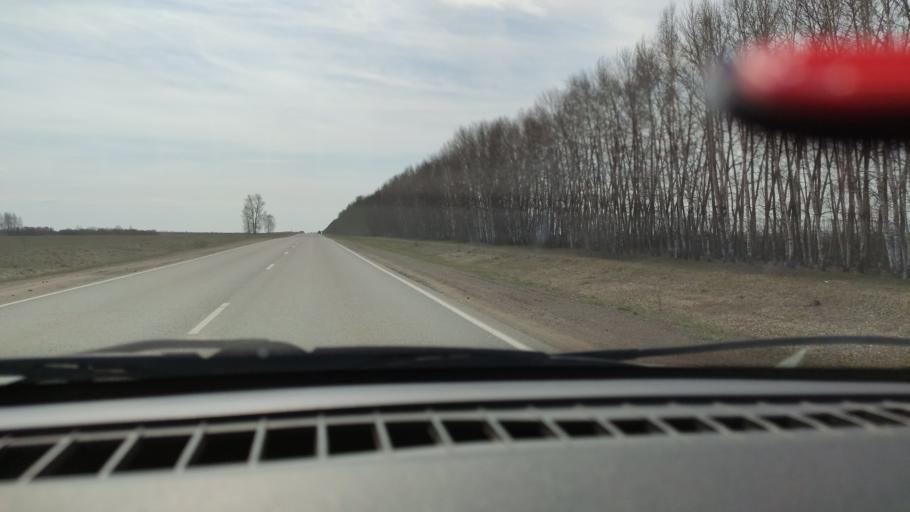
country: RU
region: Bashkortostan
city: Dyurtyuli
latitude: 55.4434
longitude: 54.8017
